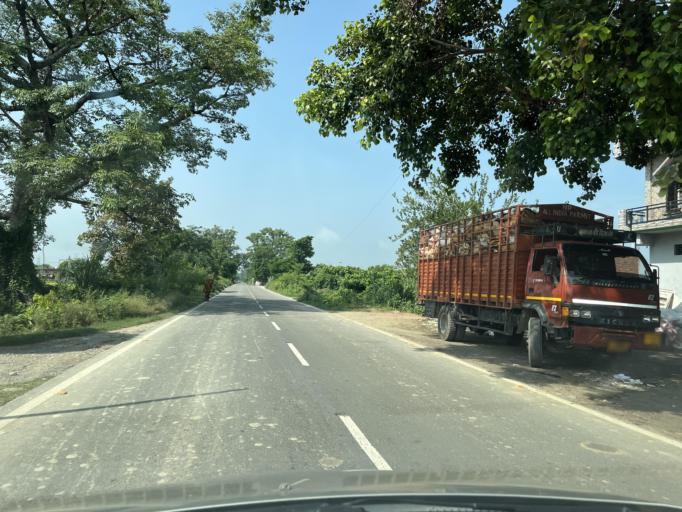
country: IN
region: Uttarakhand
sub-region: Udham Singh Nagar
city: Bazpur
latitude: 29.2005
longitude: 79.2035
